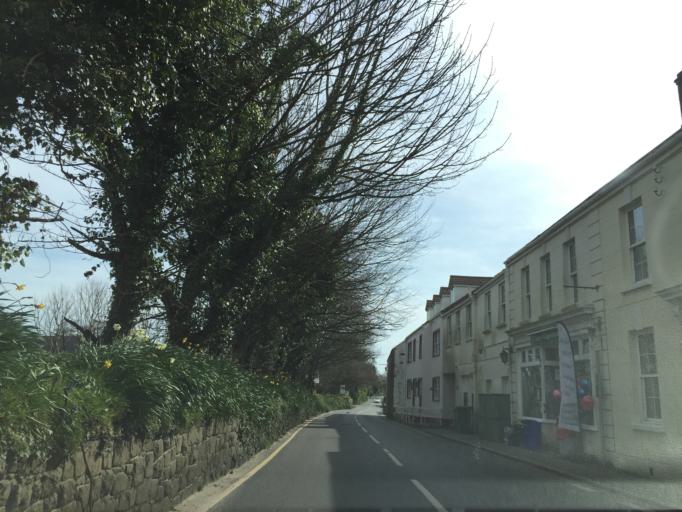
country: JE
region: St Helier
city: Saint Helier
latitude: 49.2329
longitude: -2.0889
